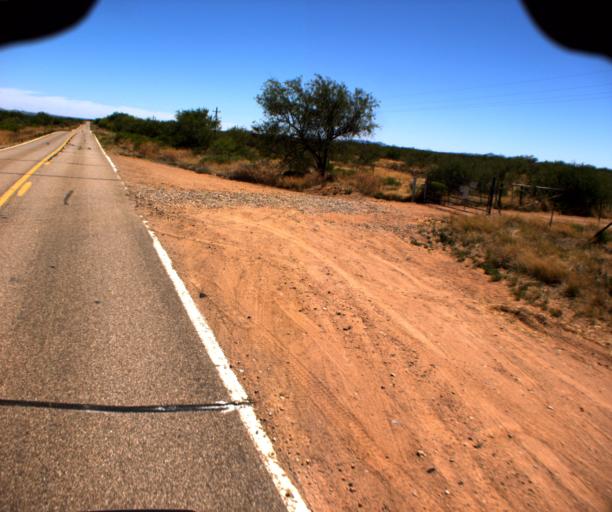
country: US
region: Arizona
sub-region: Pima County
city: Three Points
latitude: 31.7248
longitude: -111.4880
